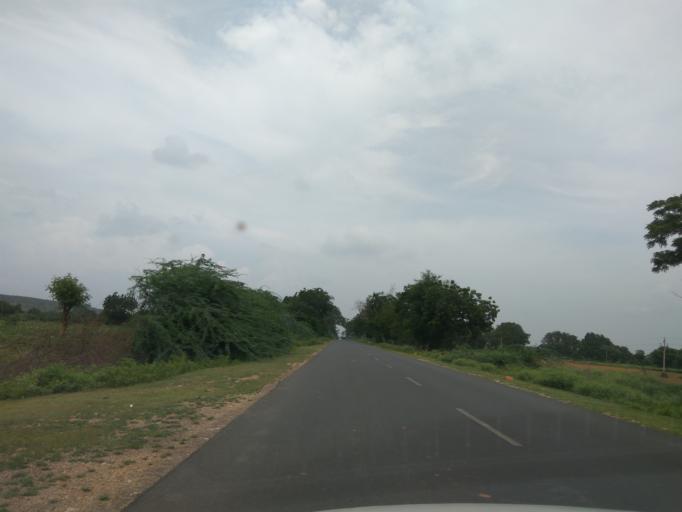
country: IN
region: Andhra Pradesh
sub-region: Prakasam
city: Cumbum
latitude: 15.5005
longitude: 79.0846
